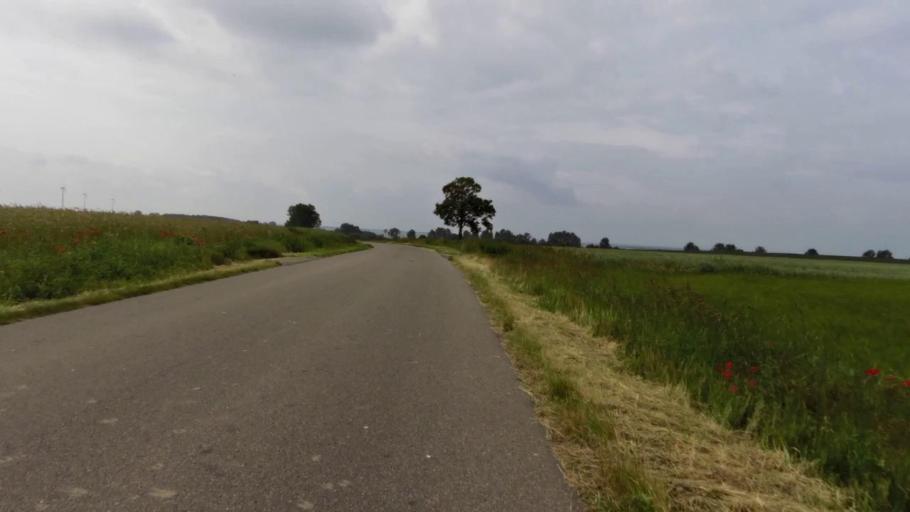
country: PL
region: West Pomeranian Voivodeship
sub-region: Powiat kamienski
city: Wolin
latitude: 53.8208
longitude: 14.6154
